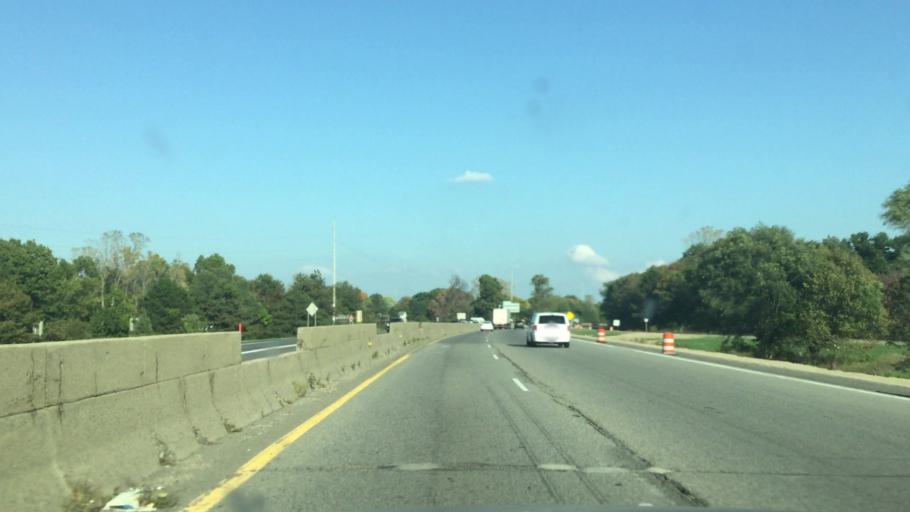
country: US
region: Michigan
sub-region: Jackson County
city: Jackson
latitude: 42.2722
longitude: -84.4261
